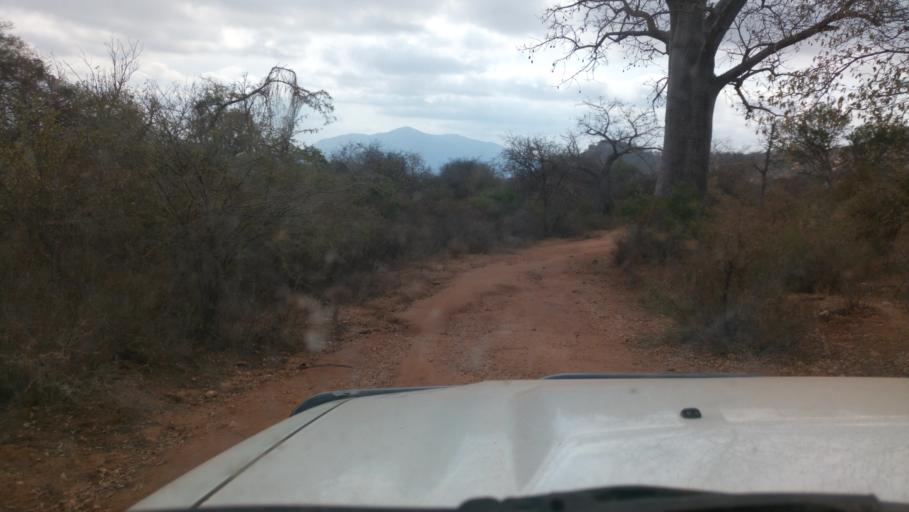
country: KE
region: Kitui
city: Kitui
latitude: -1.8431
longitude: 38.2961
